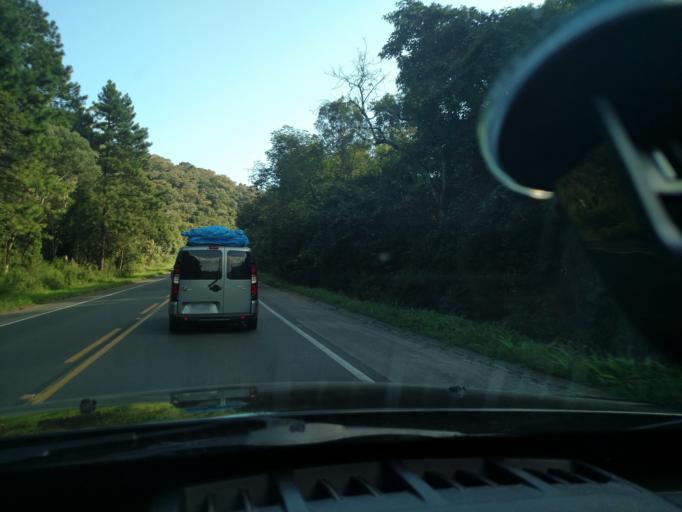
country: BR
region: Santa Catarina
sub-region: Otacilio Costa
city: Otacilio Costa
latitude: -27.2898
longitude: -50.0778
